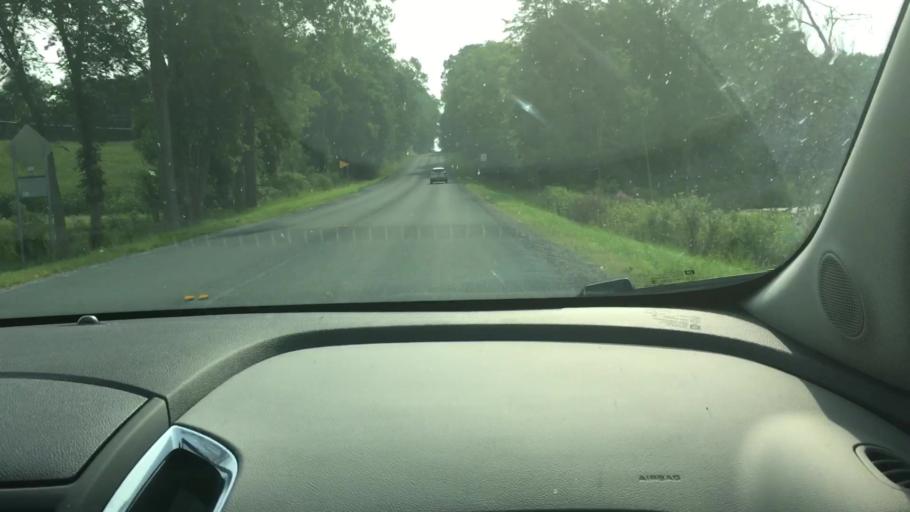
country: US
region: Michigan
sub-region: Cass County
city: Marcellus
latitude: 42.0275
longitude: -85.7125
